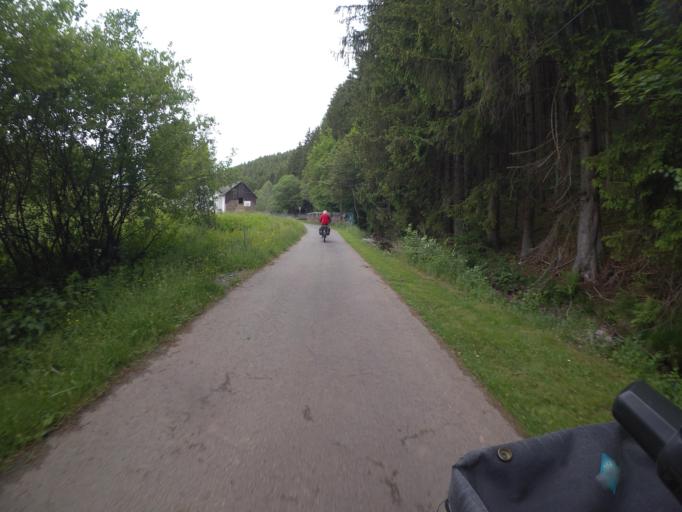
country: DE
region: North Rhine-Westphalia
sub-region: Regierungsbezirk Koln
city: Hellenthal
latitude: 50.4289
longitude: 6.4085
